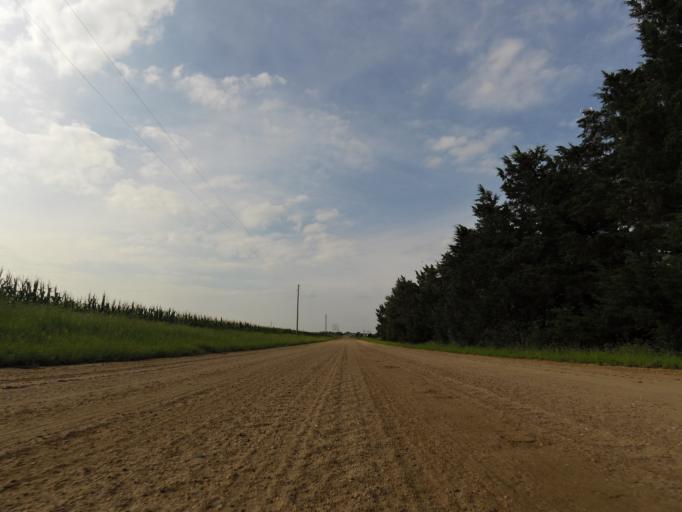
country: US
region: Kansas
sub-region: Reno County
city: South Hutchinson
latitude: 37.9741
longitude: -98.0688
